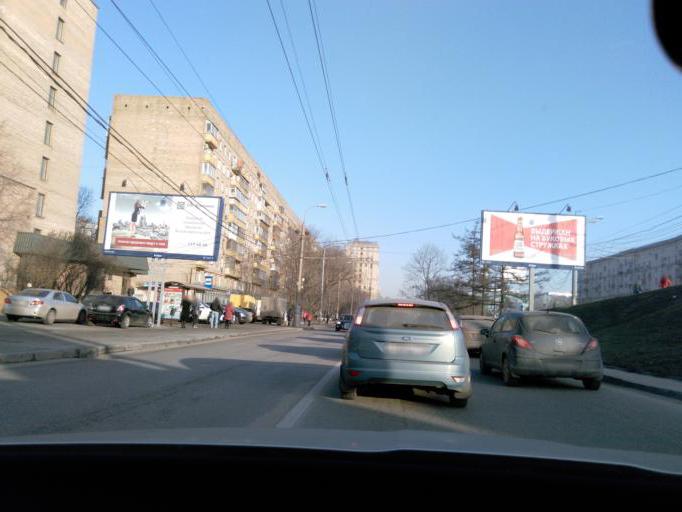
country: RU
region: Moskovskaya
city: Koptevo
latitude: 55.8155
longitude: 37.5002
